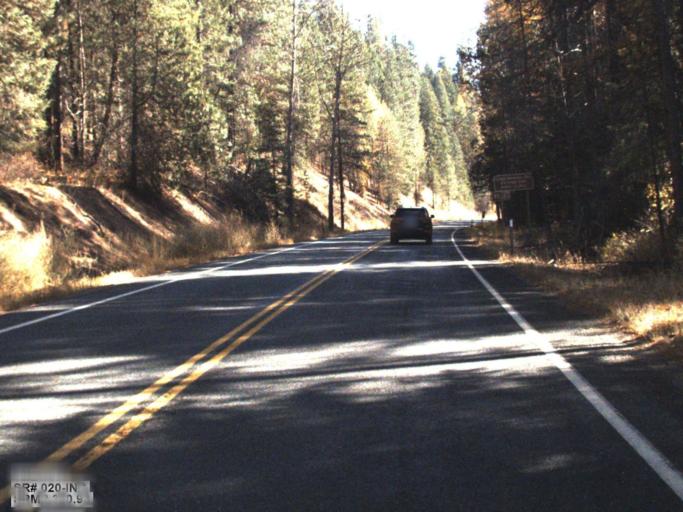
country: US
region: Washington
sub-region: Stevens County
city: Kettle Falls
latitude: 48.5892
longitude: -118.3092
